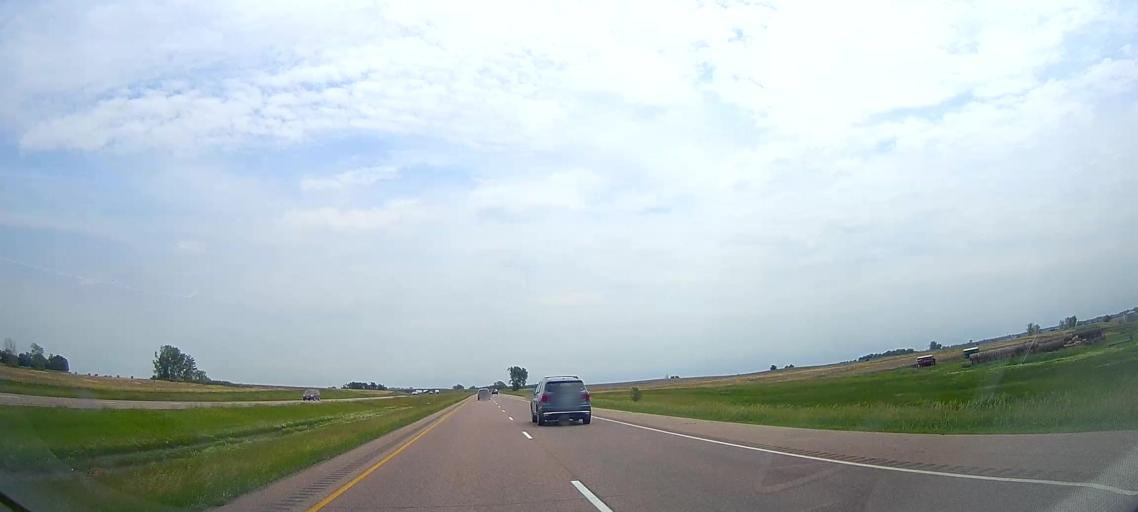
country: US
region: South Dakota
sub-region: Minnehaha County
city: Hartford
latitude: 43.6140
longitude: -97.0387
